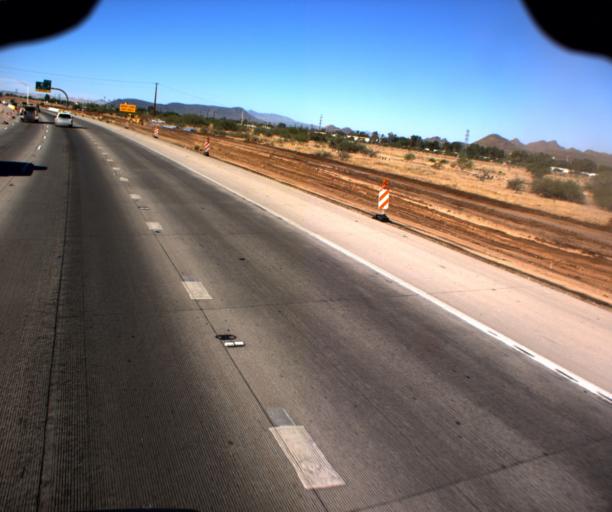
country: US
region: Arizona
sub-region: Pima County
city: South Tucson
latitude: 32.1842
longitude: -110.9850
